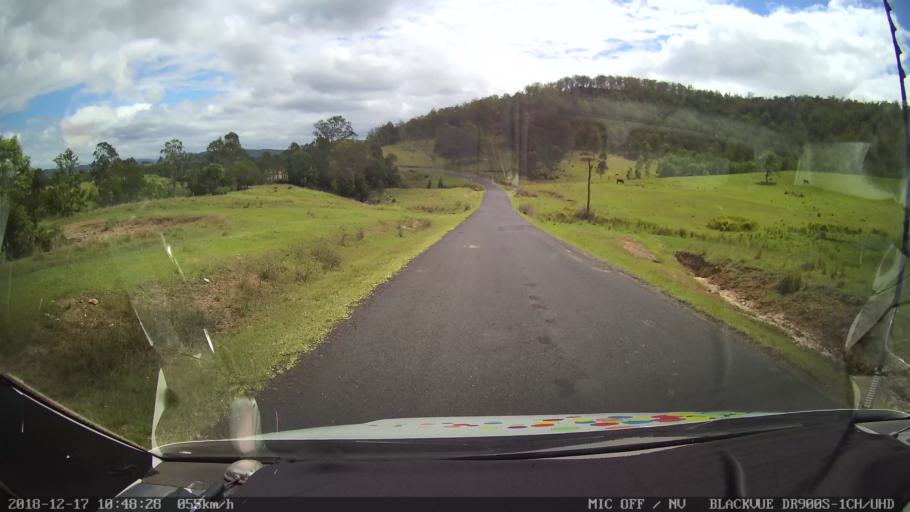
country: AU
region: New South Wales
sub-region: Clarence Valley
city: Gordon
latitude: -28.8728
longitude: 152.5710
